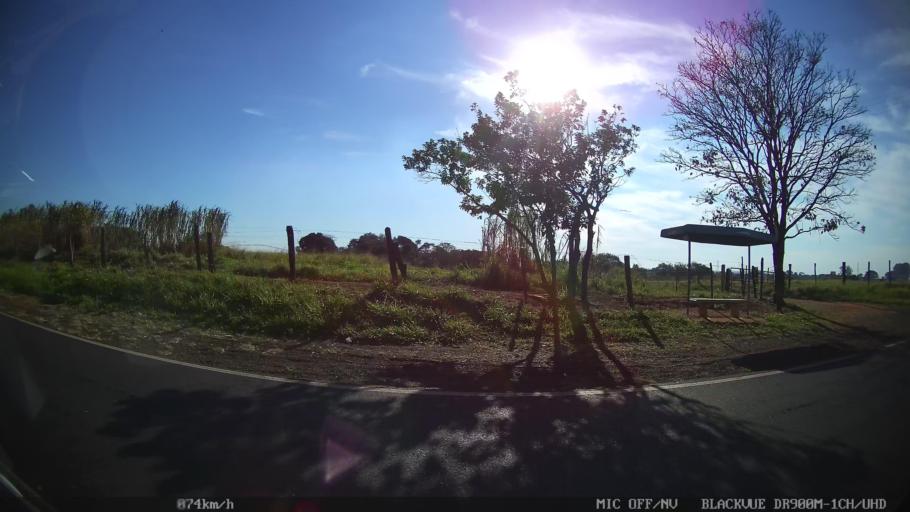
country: BR
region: Sao Paulo
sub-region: Americo Brasiliense
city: Americo Brasiliense
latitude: -21.7539
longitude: -48.1375
